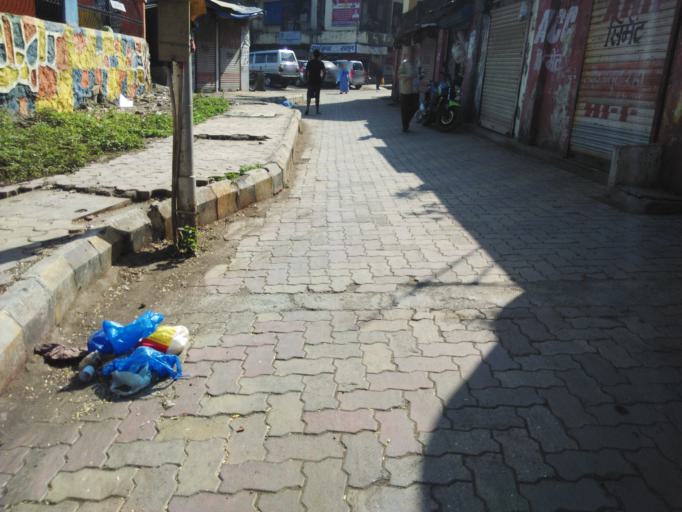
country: IN
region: Maharashtra
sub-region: Thane
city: Bhayandar
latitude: 19.3134
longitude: 72.8556
